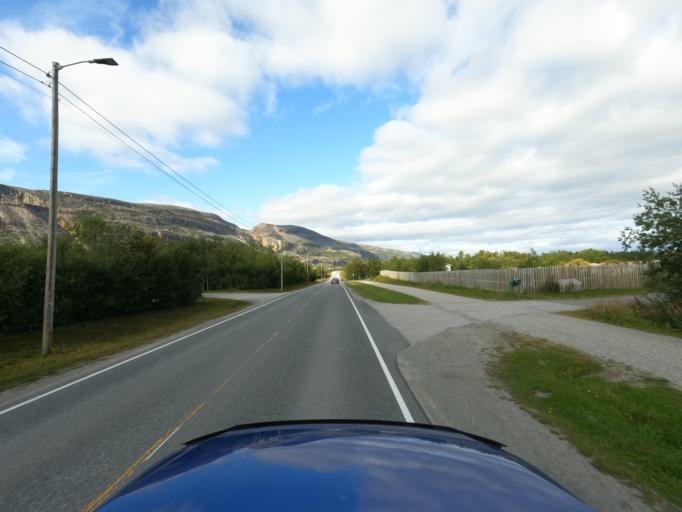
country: NO
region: Finnmark Fylke
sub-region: Porsanger
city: Lakselv
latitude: 70.0588
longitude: 24.9344
